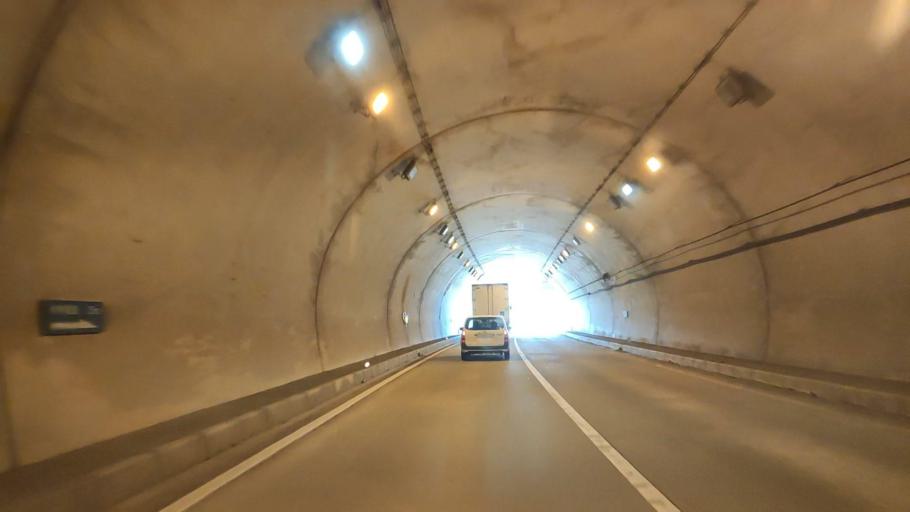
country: JP
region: Toyama
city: Yatsuomachi-higashikumisaka
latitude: 36.5309
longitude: 137.2262
